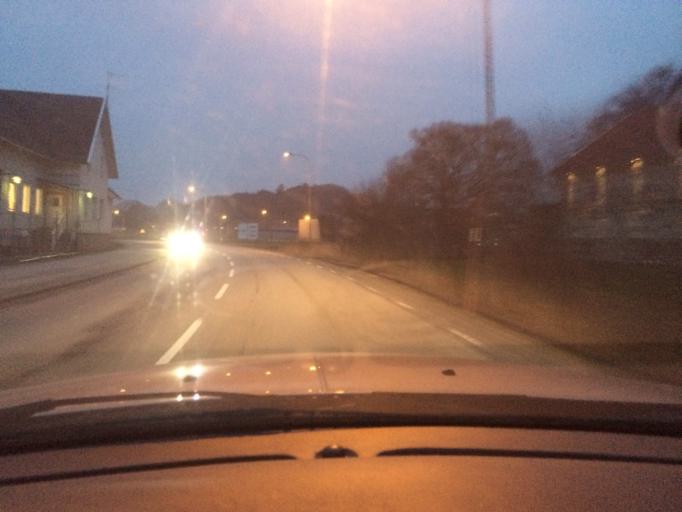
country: SE
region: Vaestra Goetaland
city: Svanesund
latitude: 58.1043
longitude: 11.8516
